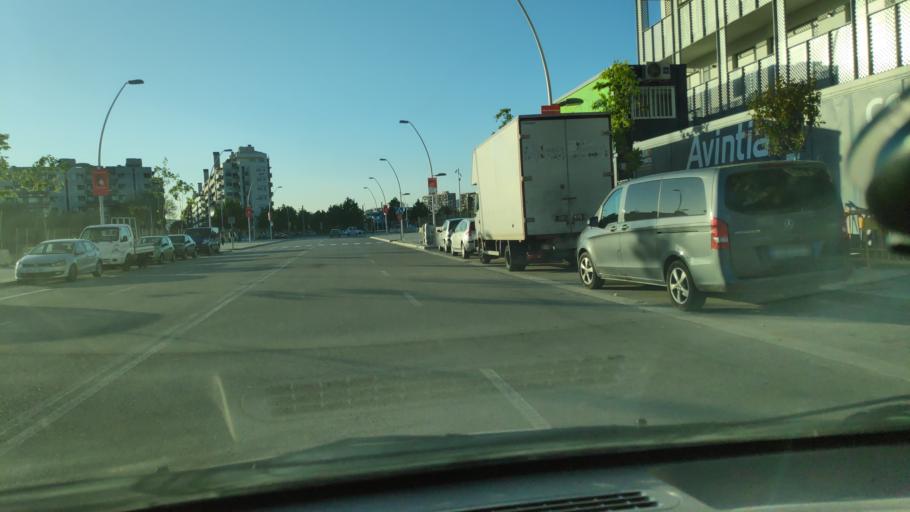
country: ES
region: Catalonia
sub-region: Provincia de Barcelona
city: Sant Adria de Besos
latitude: 41.4217
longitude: 2.2236
